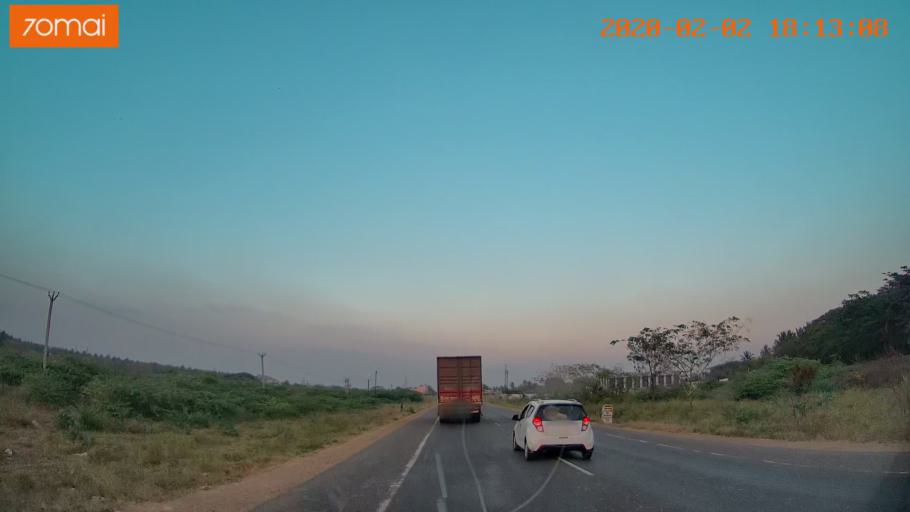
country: IN
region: Tamil Nadu
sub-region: Coimbatore
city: Singanallur
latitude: 10.9874
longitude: 77.0530
